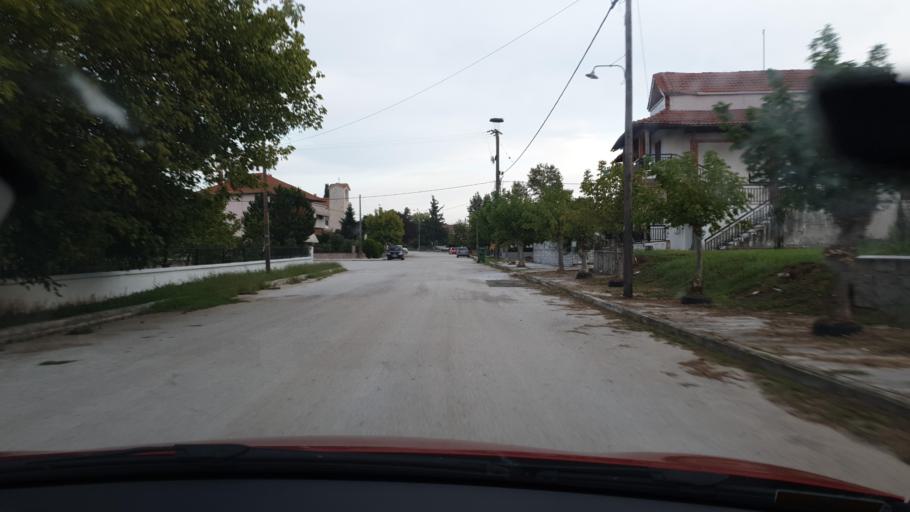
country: GR
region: Central Macedonia
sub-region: Nomos Kilkis
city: Kristoni
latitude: 40.9529
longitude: 22.8222
